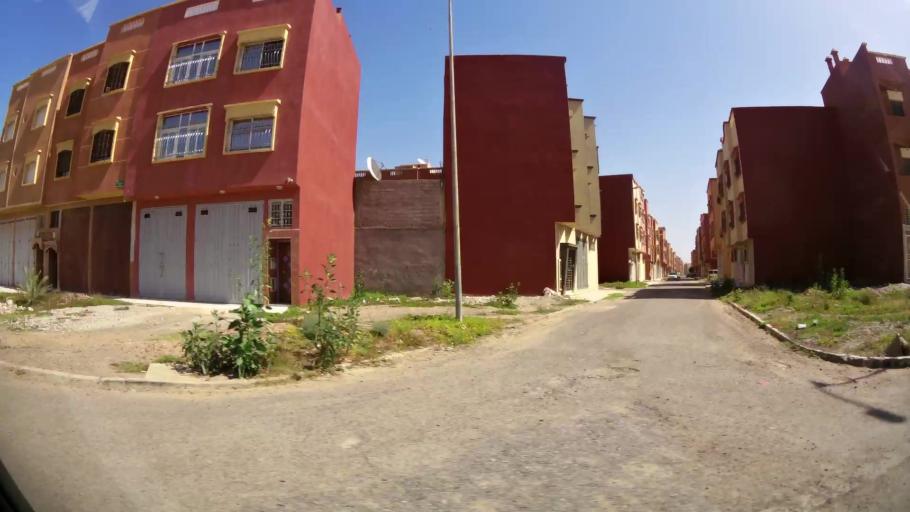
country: MA
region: Souss-Massa-Draa
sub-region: Inezgane-Ait Mellou
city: Inezgane
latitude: 30.3281
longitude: -9.5098
